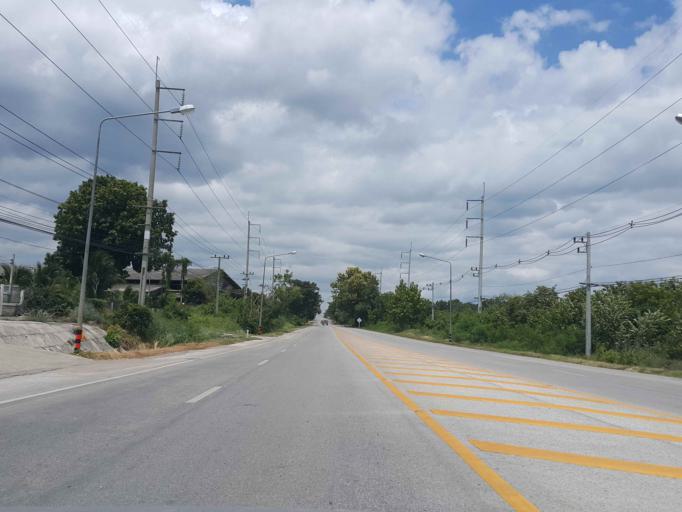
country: TH
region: Lamphun
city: Ban Hong
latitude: 18.3612
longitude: 98.8110
